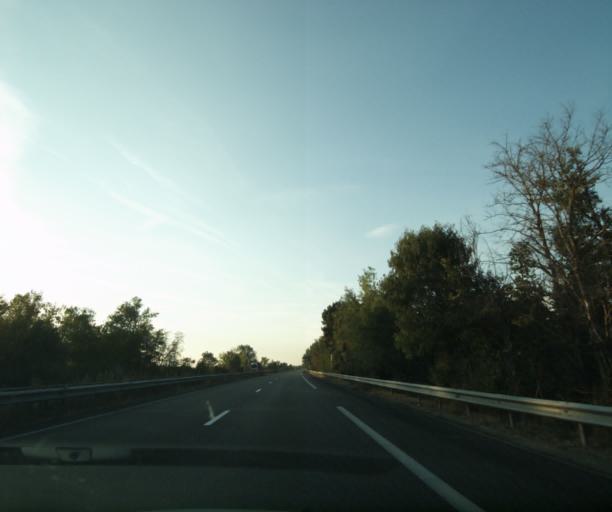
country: FR
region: Aquitaine
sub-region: Departement du Lot-et-Garonne
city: Layrac
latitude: 44.1349
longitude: 0.6753
